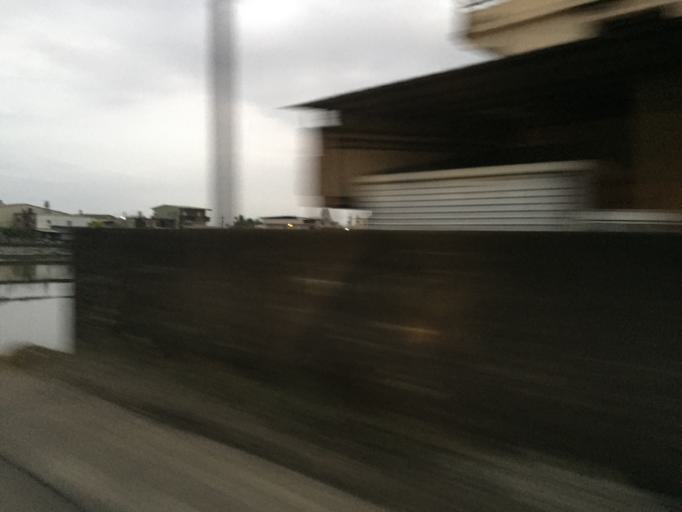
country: TW
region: Taiwan
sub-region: Yilan
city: Yilan
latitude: 24.7716
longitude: 121.7446
